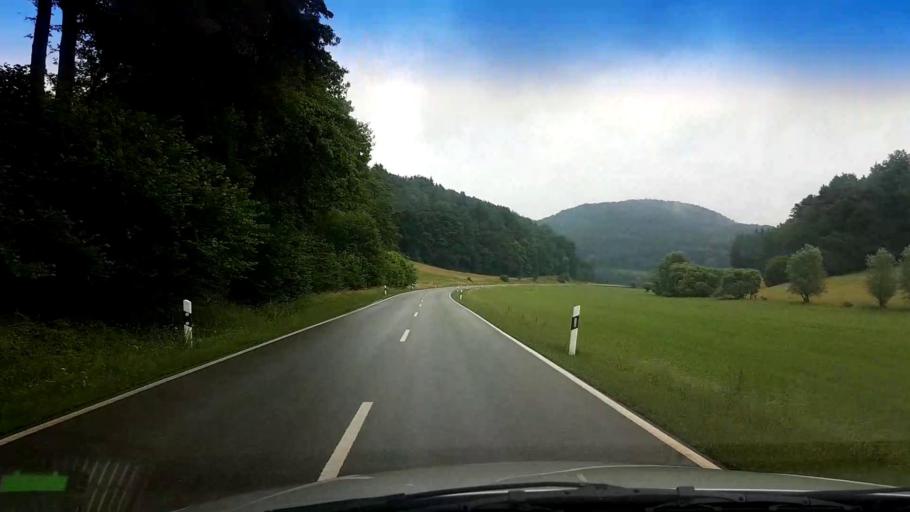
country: DE
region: Bavaria
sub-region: Upper Franconia
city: Weismain
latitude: 50.0717
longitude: 11.2094
